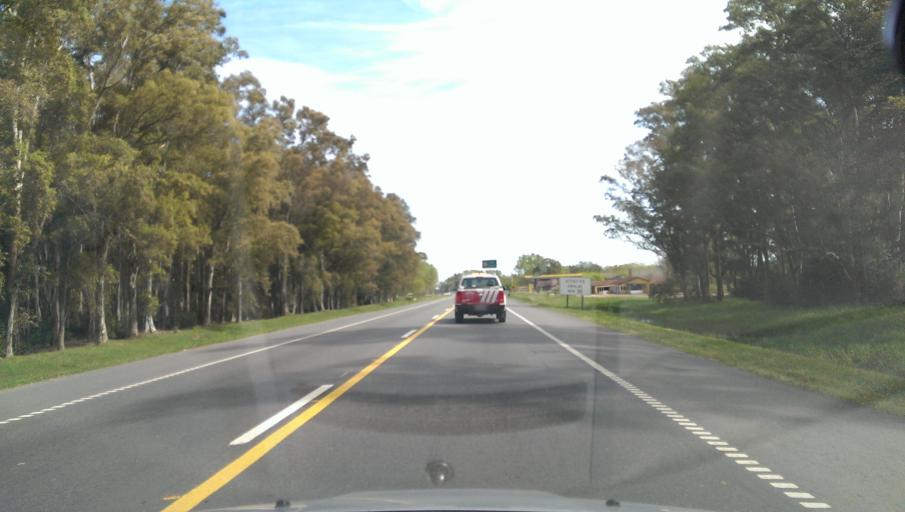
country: AR
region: Buenos Aires
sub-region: Partido de Las Flores
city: Las Flores
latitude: -36.3838
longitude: -59.4877
